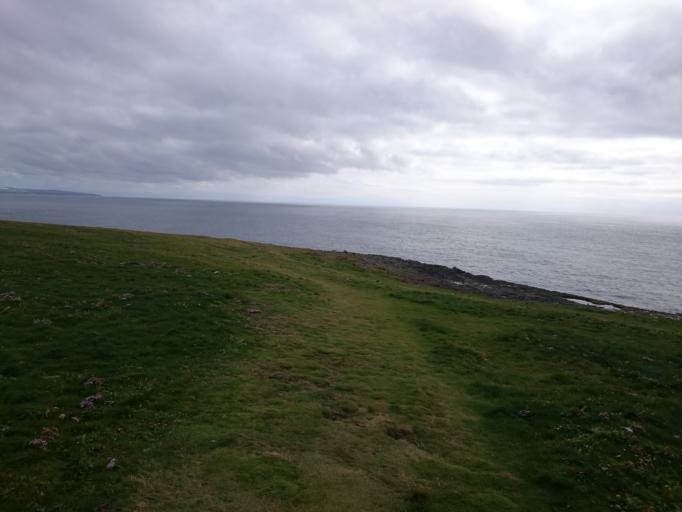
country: IE
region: Munster
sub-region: Ciarrai
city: Ballybunnion
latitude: 52.5596
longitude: -9.9377
